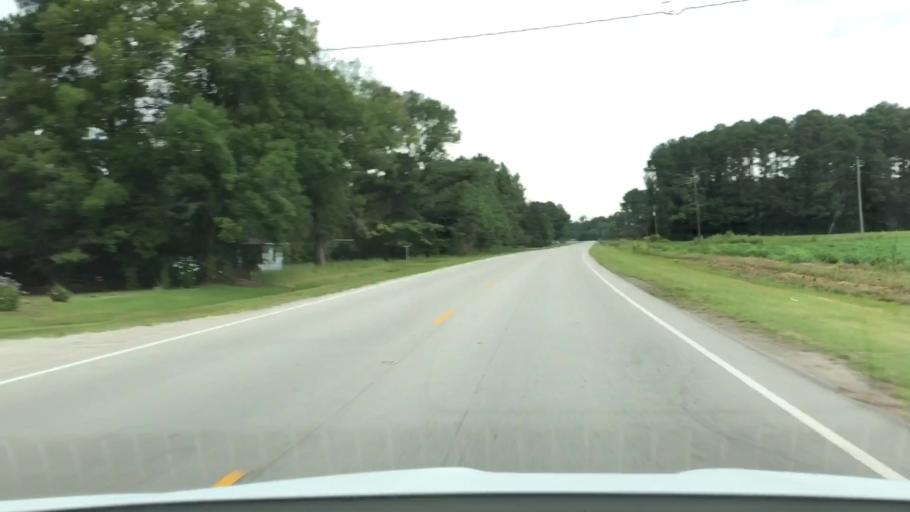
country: US
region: North Carolina
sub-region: Jones County
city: Trenton
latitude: 35.0214
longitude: -77.3044
